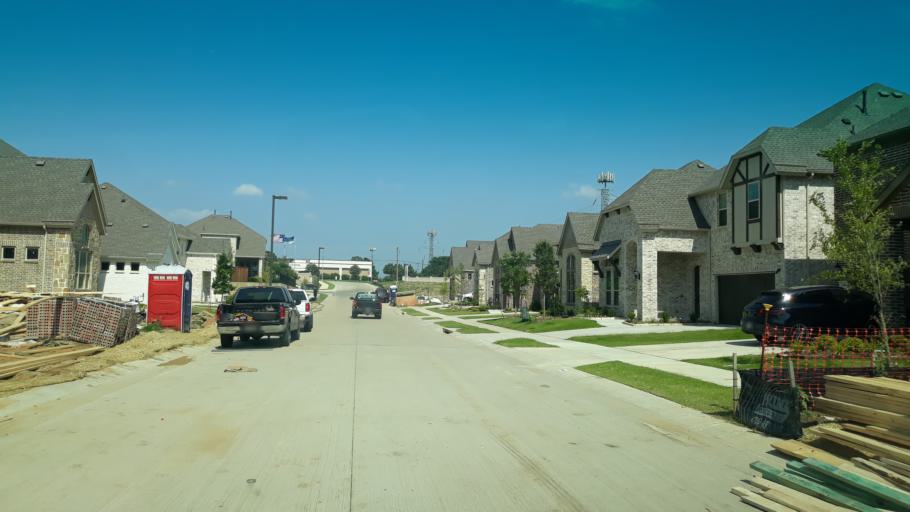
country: US
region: Texas
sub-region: Dallas County
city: Irving
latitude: 32.8693
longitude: -96.9940
